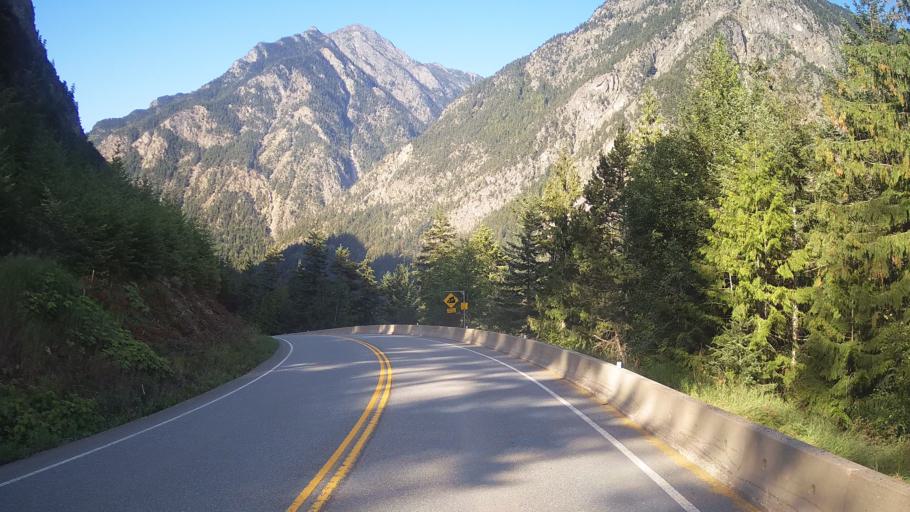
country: CA
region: British Columbia
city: Lillooet
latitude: 50.6307
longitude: -122.0914
